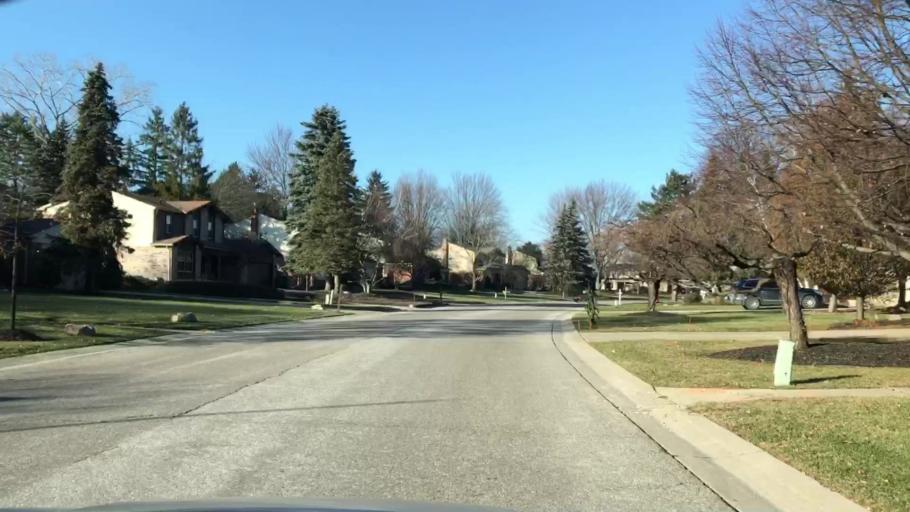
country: US
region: Michigan
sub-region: Wayne County
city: Northville
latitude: 42.4474
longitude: -83.4843
